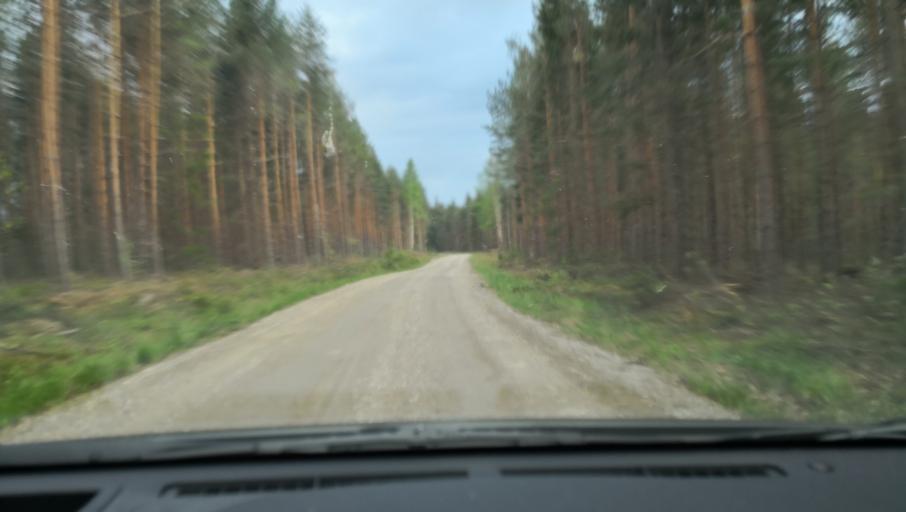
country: SE
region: Vaestmanland
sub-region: Skinnskattebergs Kommun
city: Skinnskatteberg
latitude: 59.7884
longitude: 15.4473
